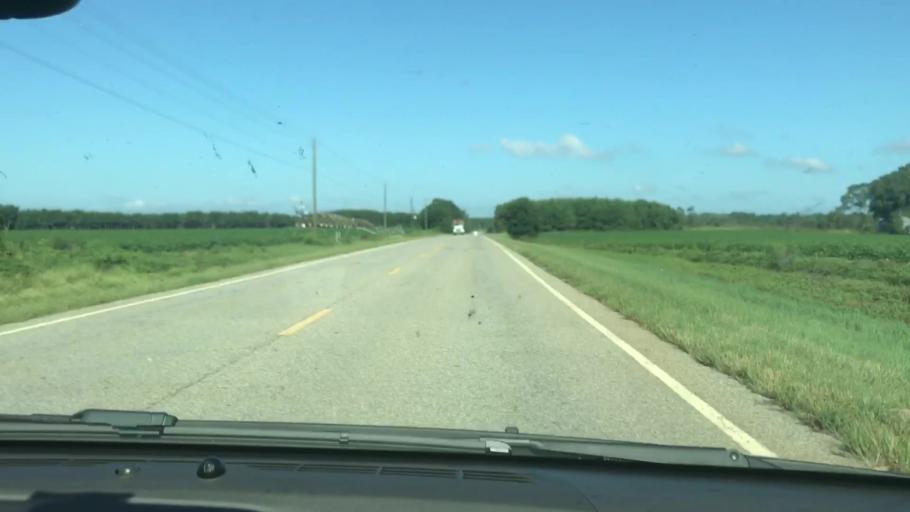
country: US
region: Georgia
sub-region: Quitman County
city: Georgetown
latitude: 31.7615
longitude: -85.0761
